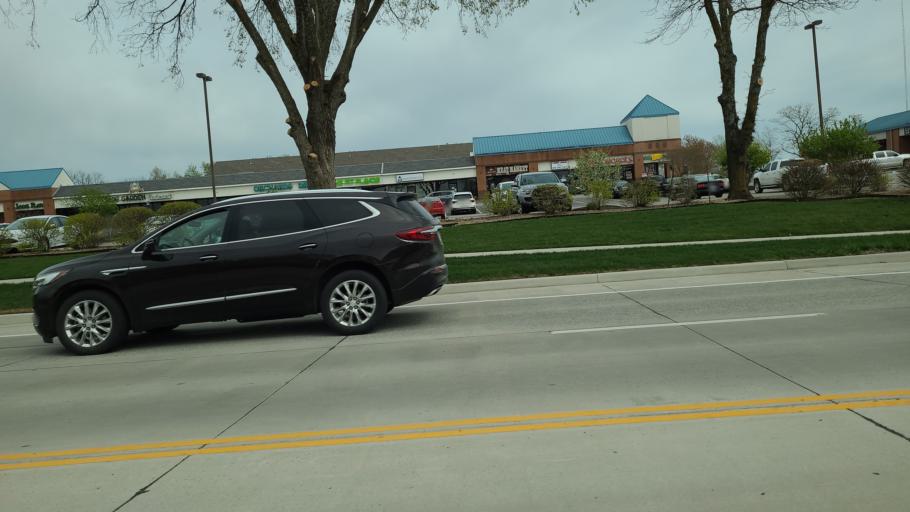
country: US
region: Kansas
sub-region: Douglas County
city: Lawrence
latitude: 38.9583
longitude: -95.2790
